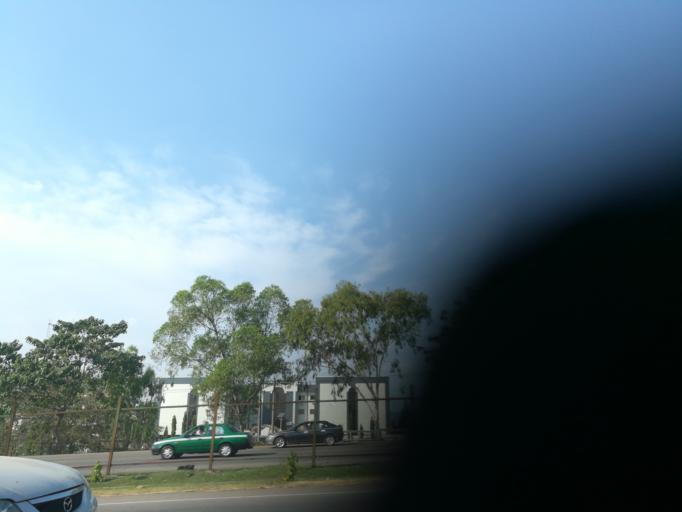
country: NG
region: Abuja Federal Capital Territory
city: Abuja
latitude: 9.0787
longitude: 7.4523
